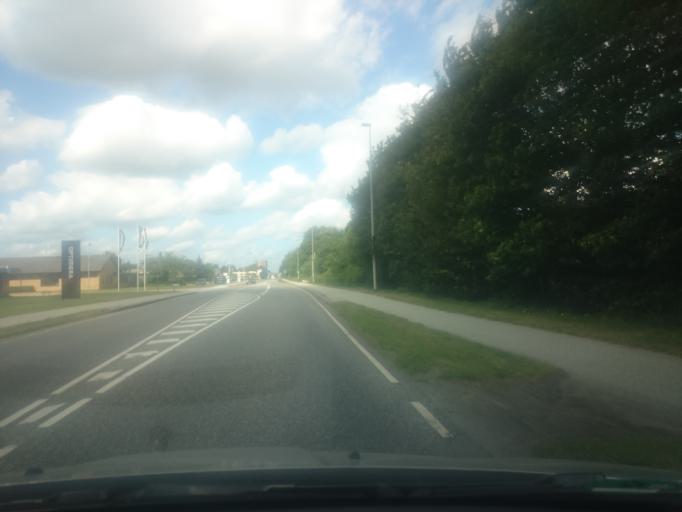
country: DK
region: South Denmark
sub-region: Billund Kommune
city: Billund
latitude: 55.7266
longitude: 9.1258
